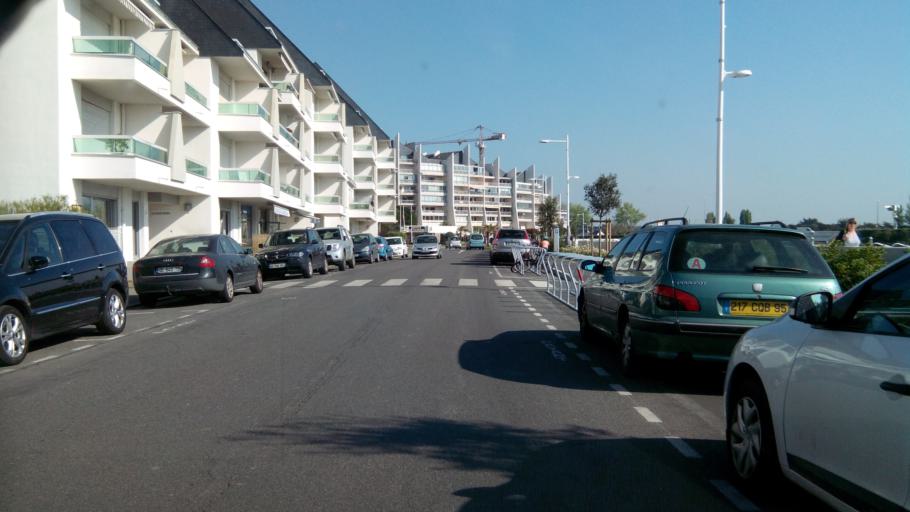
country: FR
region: Pays de la Loire
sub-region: Departement de la Loire-Atlantique
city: Le Pouliguen
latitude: 47.2791
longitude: -2.4281
